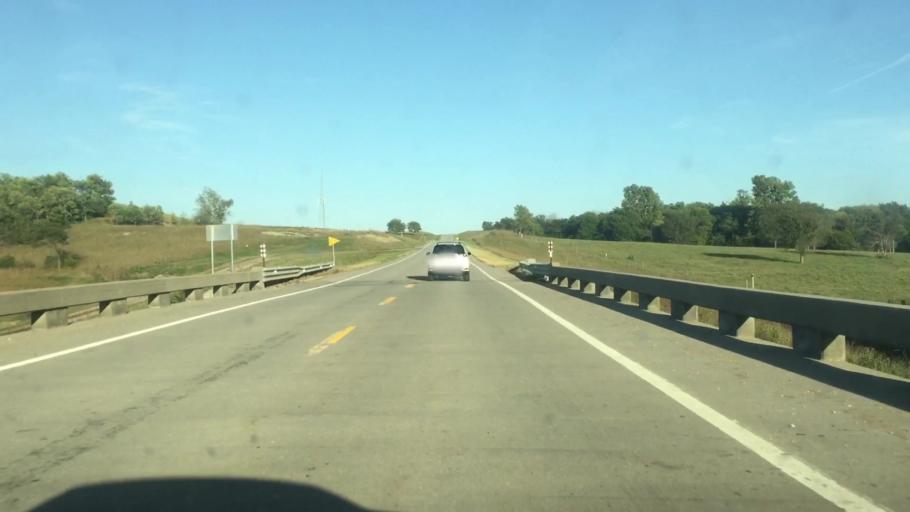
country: US
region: Kansas
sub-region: Brown County
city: Horton
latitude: 39.5875
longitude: -95.5547
